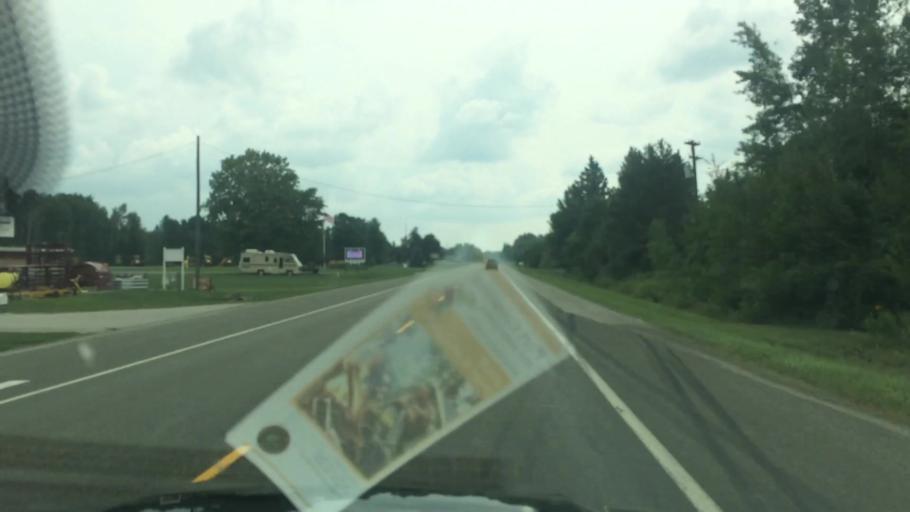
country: US
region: Michigan
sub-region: Tuscola County
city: Cass City
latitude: 43.6607
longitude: -83.0983
